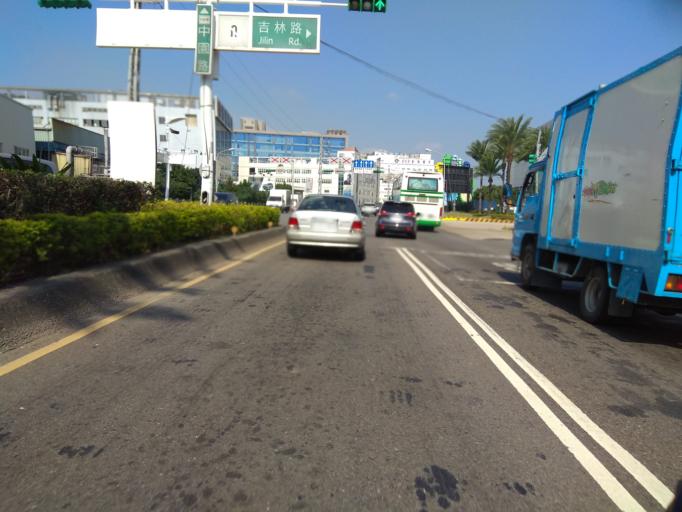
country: TW
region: Taiwan
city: Taoyuan City
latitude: 24.9810
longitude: 121.2364
